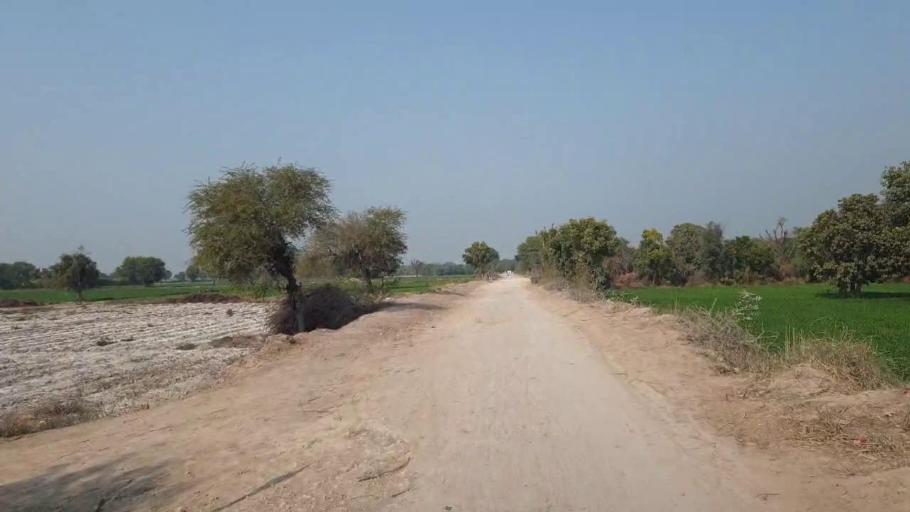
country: PK
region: Sindh
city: Hala
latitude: 25.8681
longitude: 68.4618
